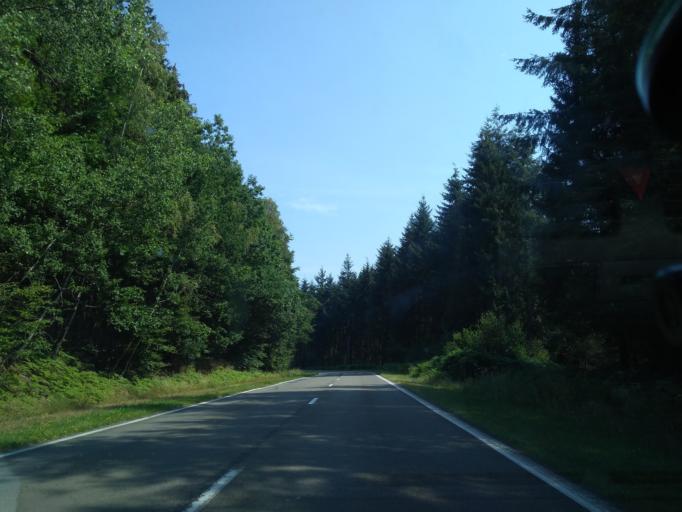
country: BE
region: Wallonia
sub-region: Province du Luxembourg
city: Tenneville
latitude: 50.1400
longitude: 5.5002
